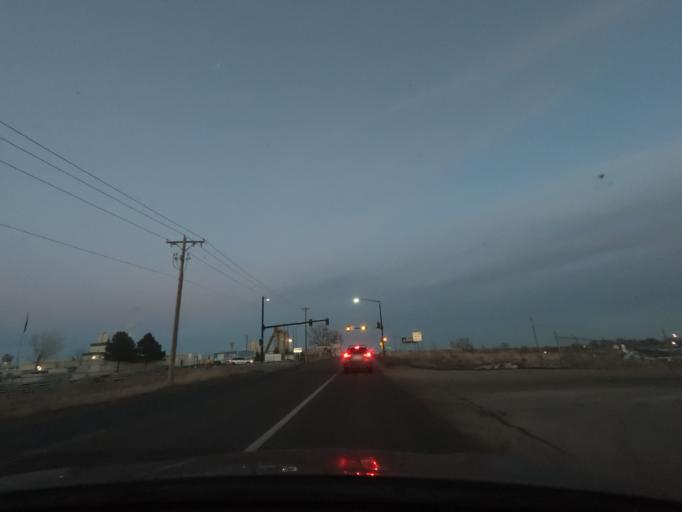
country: US
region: Colorado
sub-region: El Paso County
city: Stratmoor
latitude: 38.7773
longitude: -104.7731
